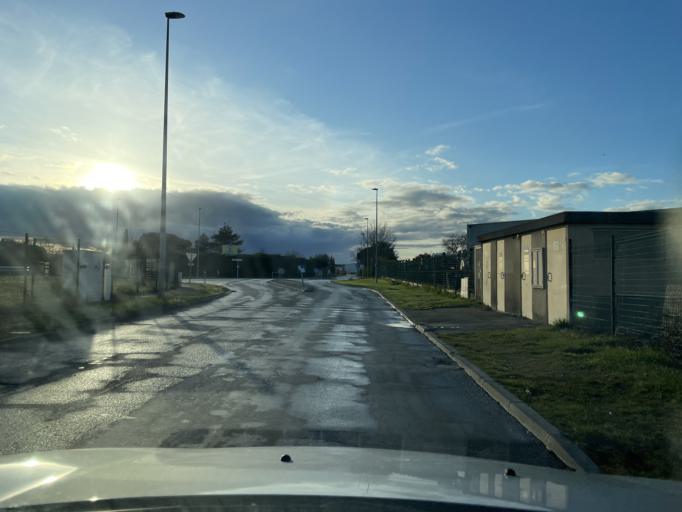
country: FR
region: Midi-Pyrenees
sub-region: Departement de la Haute-Garonne
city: Tournefeuille
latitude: 43.6003
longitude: 1.3085
